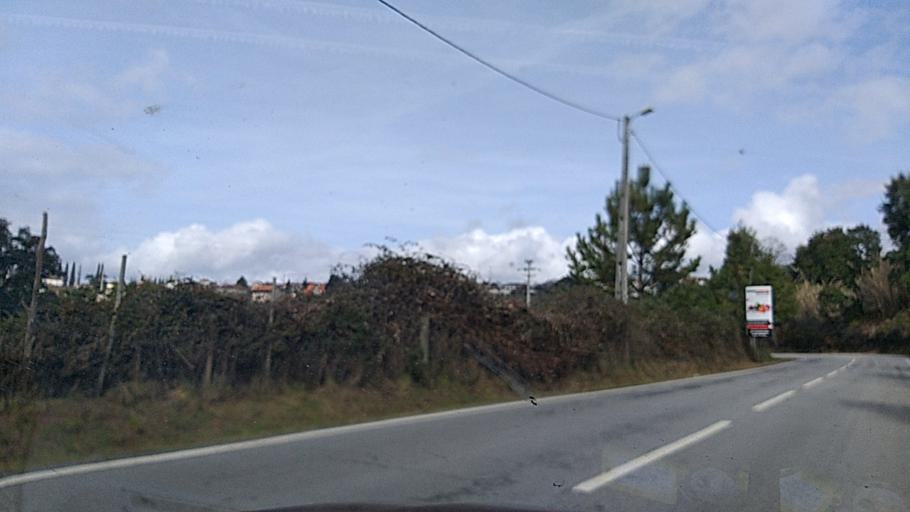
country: PT
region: Viseu
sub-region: Satao
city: Satao
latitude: 40.6706
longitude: -7.6944
